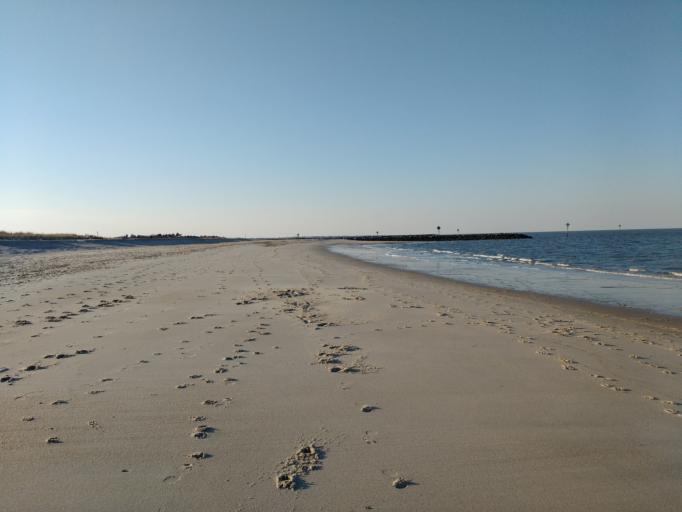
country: US
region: Delaware
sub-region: Sussex County
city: Lewes
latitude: 38.7895
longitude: -75.1564
